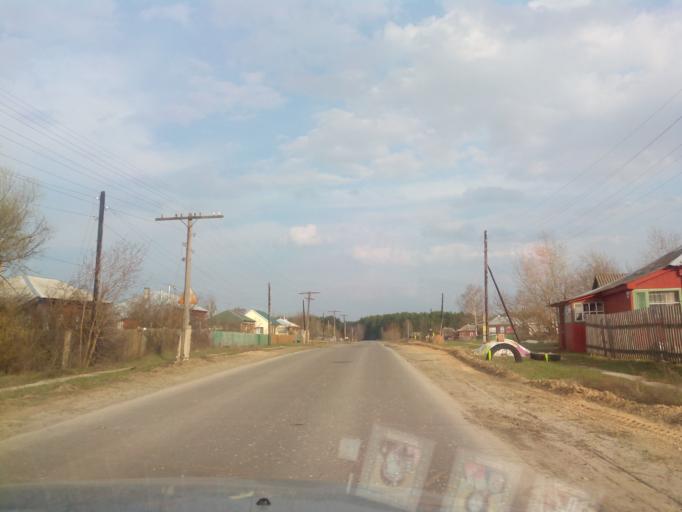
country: RU
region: Rjazan
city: Spassk-Ryazanskiy
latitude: 54.4706
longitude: 40.5319
